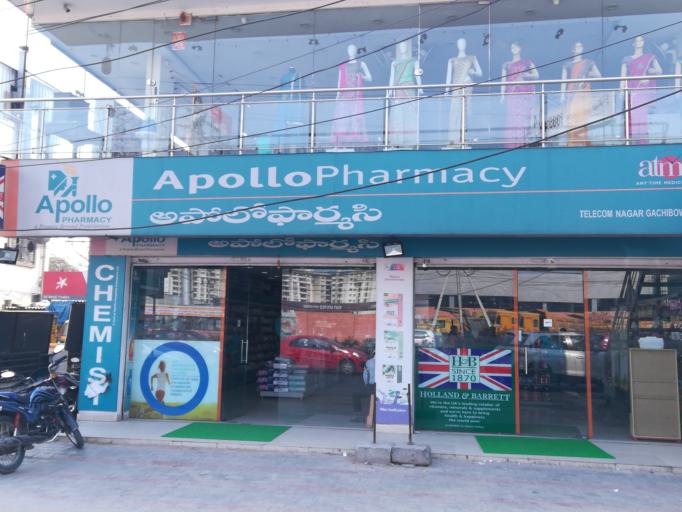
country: IN
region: Telangana
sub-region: Rangareddi
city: Kukatpalli
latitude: 17.4340
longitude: 78.3689
